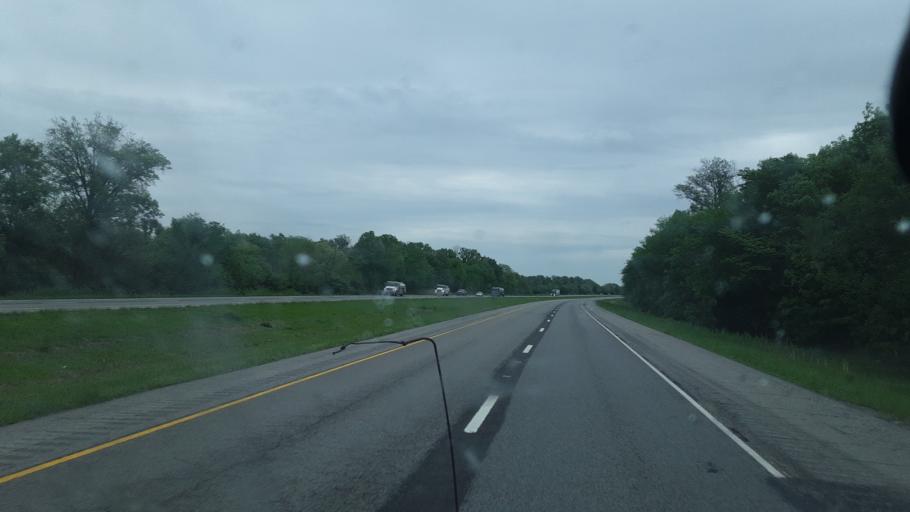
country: US
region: Illinois
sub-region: Wayne County
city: Wayne City
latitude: 38.2716
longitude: -88.6941
